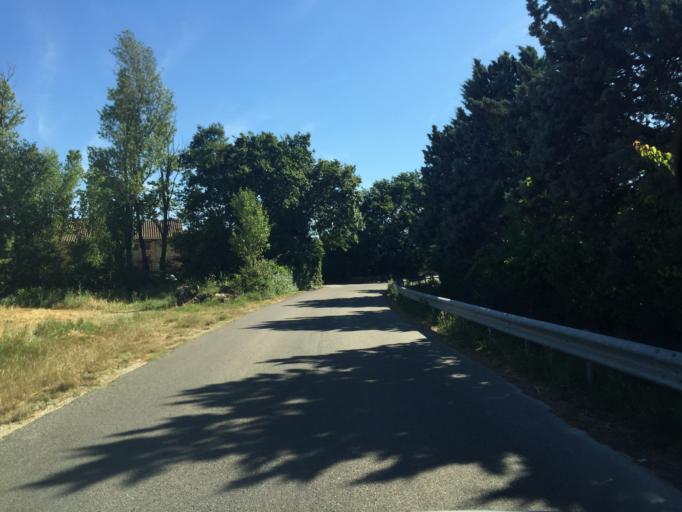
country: FR
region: Provence-Alpes-Cote d'Azur
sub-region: Departement du Vaucluse
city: Caderousse
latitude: 44.1081
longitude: 4.7616
